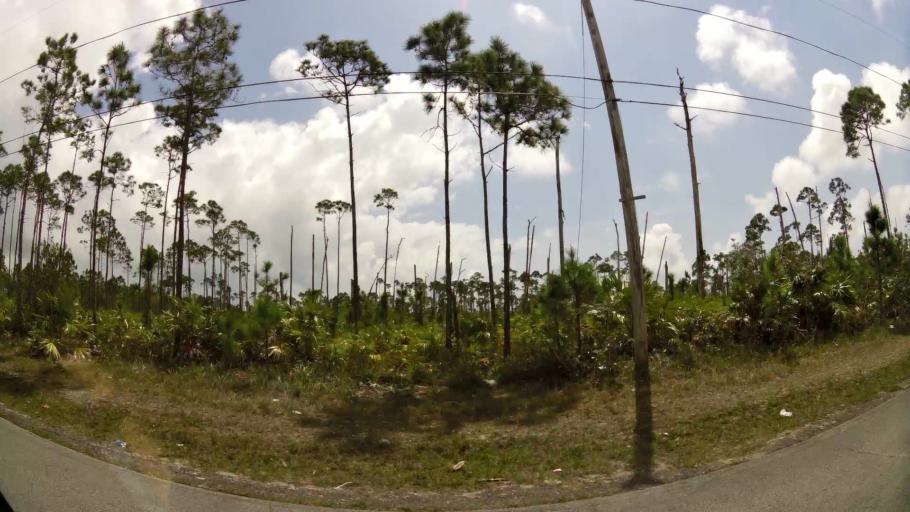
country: BS
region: Freeport
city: Lucaya
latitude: 26.5419
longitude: -78.6427
